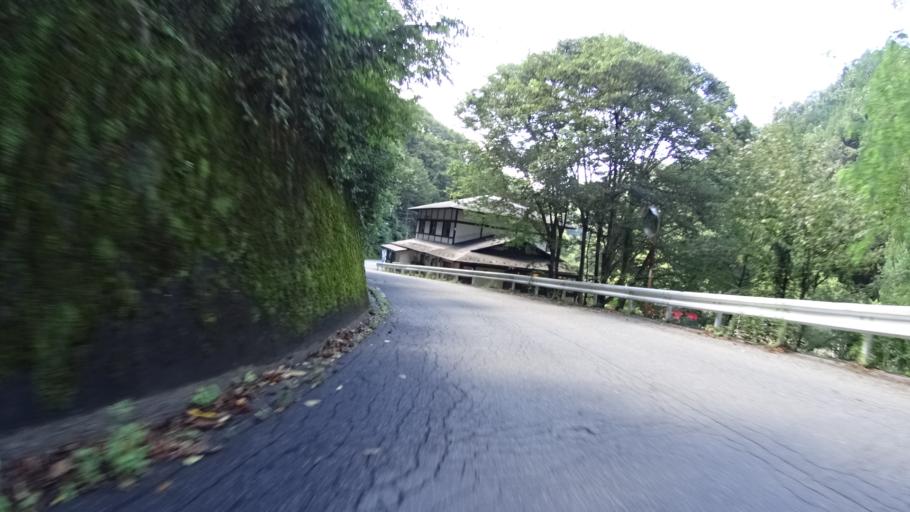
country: JP
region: Yamanashi
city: Enzan
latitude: 35.6516
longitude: 138.8160
